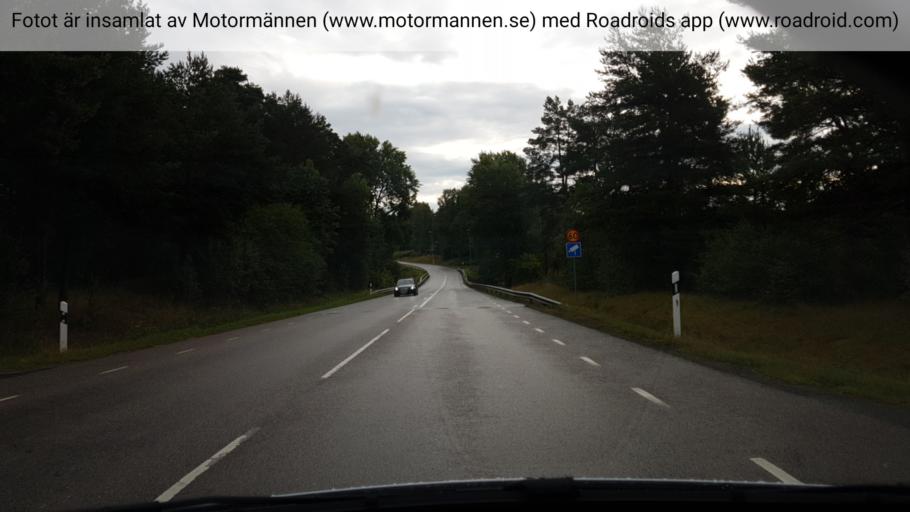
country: SE
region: Vaestra Goetaland
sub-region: Skovde Kommun
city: Stopen
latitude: 58.4337
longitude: 13.9238
